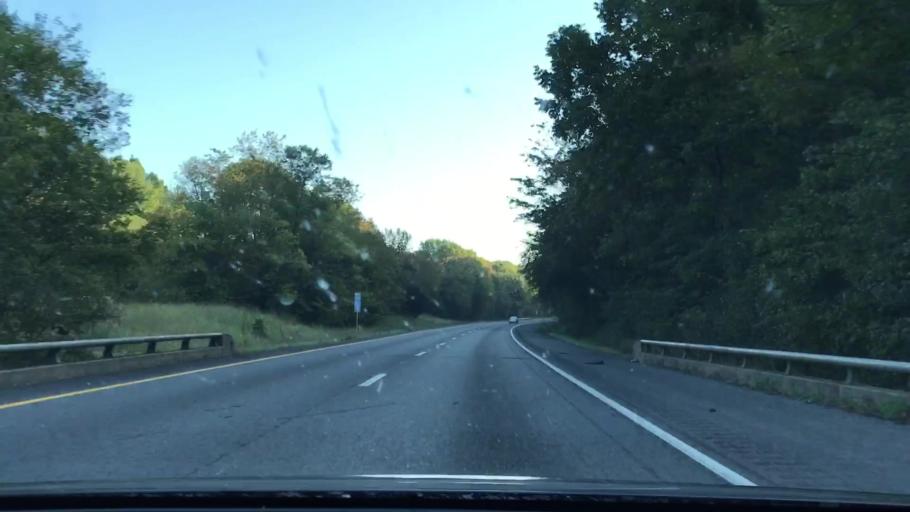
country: US
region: Tennessee
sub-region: Robertson County
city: Cross Plains
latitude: 36.5816
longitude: -86.6113
